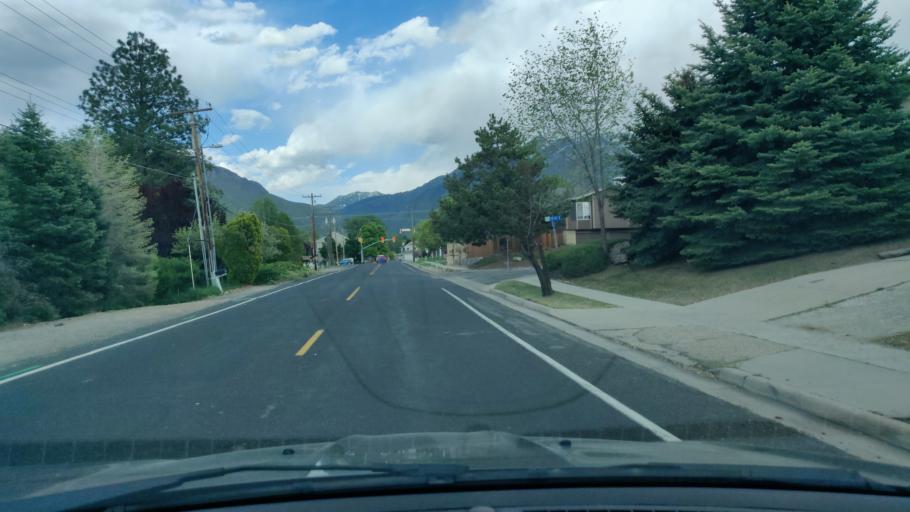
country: US
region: Utah
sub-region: Salt Lake County
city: Little Cottonwood Creek Valley
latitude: 40.6204
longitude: -111.8364
